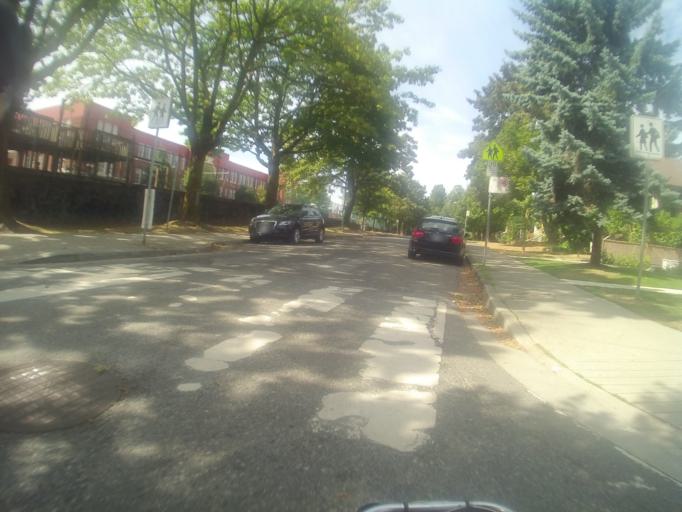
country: CA
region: British Columbia
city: West End
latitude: 49.2628
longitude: -123.1483
